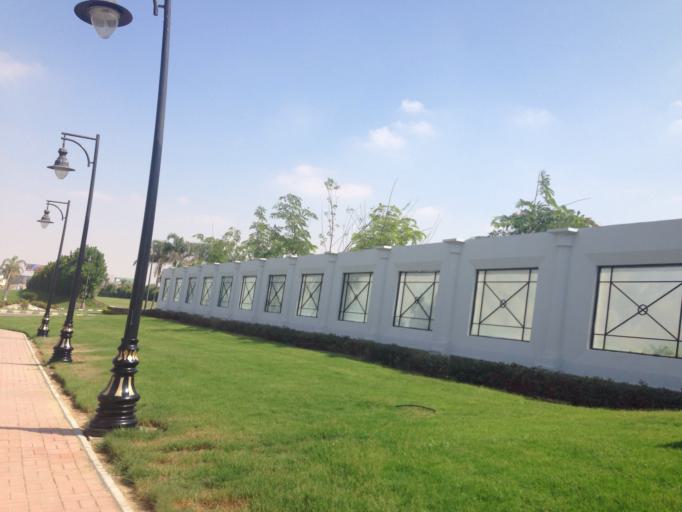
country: EG
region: Muhafazat al Qalyubiyah
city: Al Khankah
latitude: 30.0611
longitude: 31.4184
